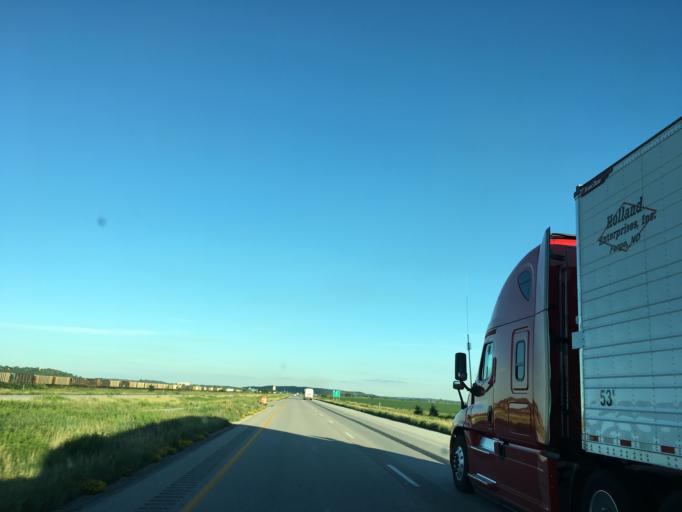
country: US
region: Iowa
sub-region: Fremont County
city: Hamburg
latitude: 40.6181
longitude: -95.6995
